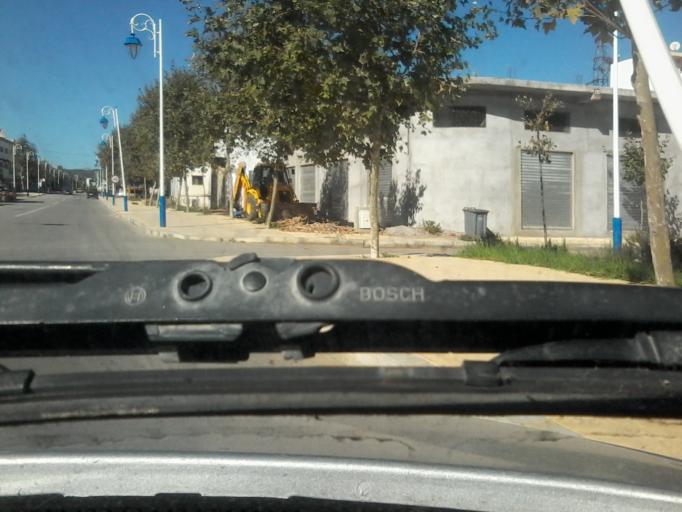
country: MA
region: Tanger-Tetouan
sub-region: Tetouan
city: Martil
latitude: 35.6966
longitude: -5.3456
